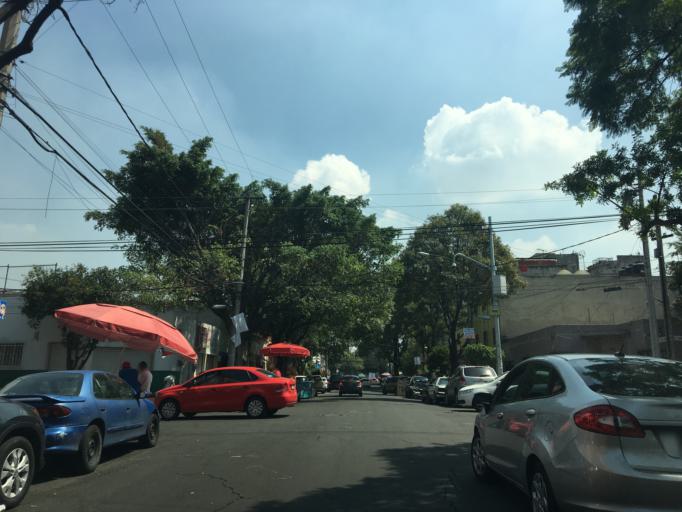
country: MX
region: Mexico City
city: Benito Juarez
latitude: 19.4063
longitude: -99.1390
